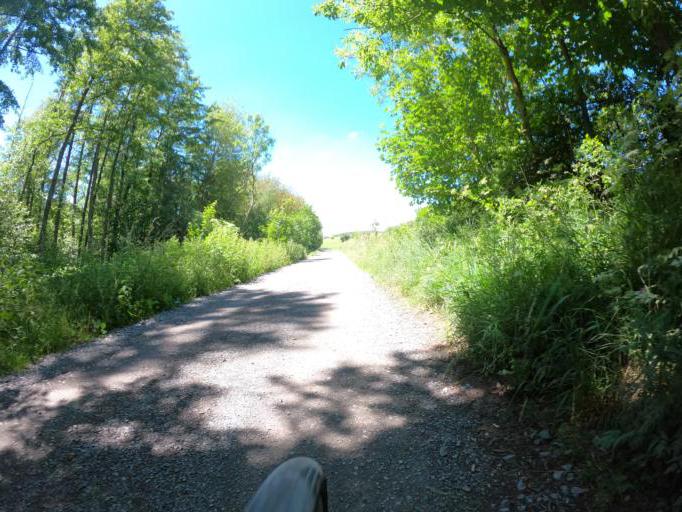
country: DE
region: Baden-Wuerttemberg
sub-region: Regierungsbezirk Stuttgart
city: Pfaffenhofen
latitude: 49.0158
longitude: 8.9796
